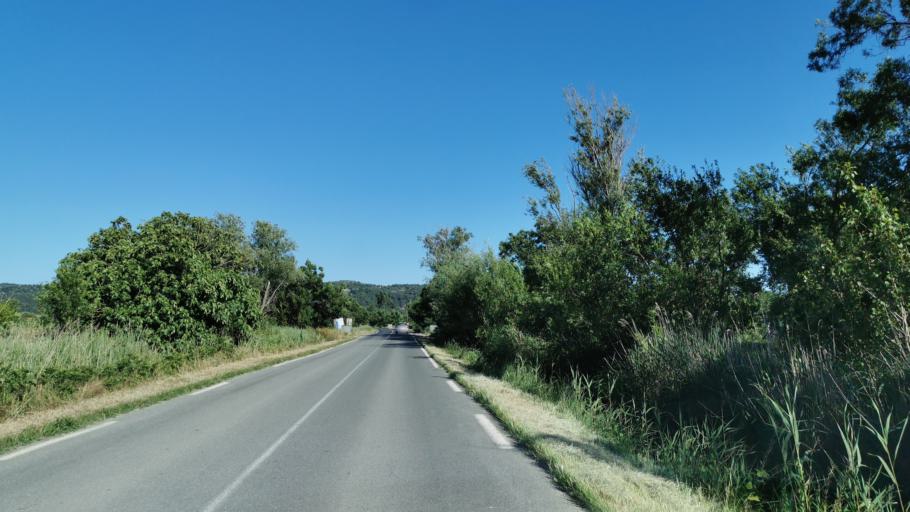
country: FR
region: Languedoc-Roussillon
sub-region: Departement de l'Aude
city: Narbonne
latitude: 43.1669
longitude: 3.0424
